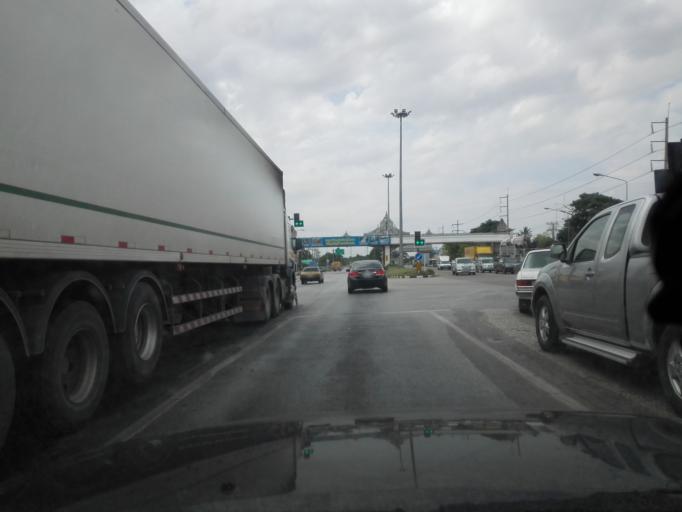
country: TH
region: Kamphaeng Phet
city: Kamphaeng Phet
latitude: 16.4742
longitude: 99.4963
